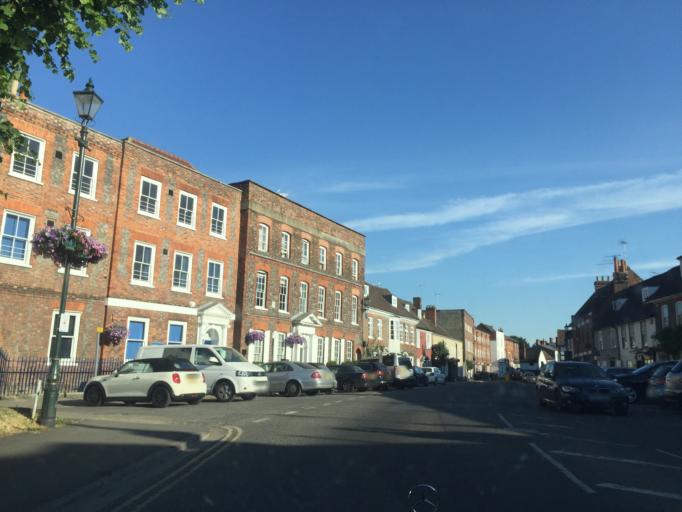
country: GB
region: England
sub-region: Oxfordshire
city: Henley on Thames
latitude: 51.5408
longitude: -0.9045
